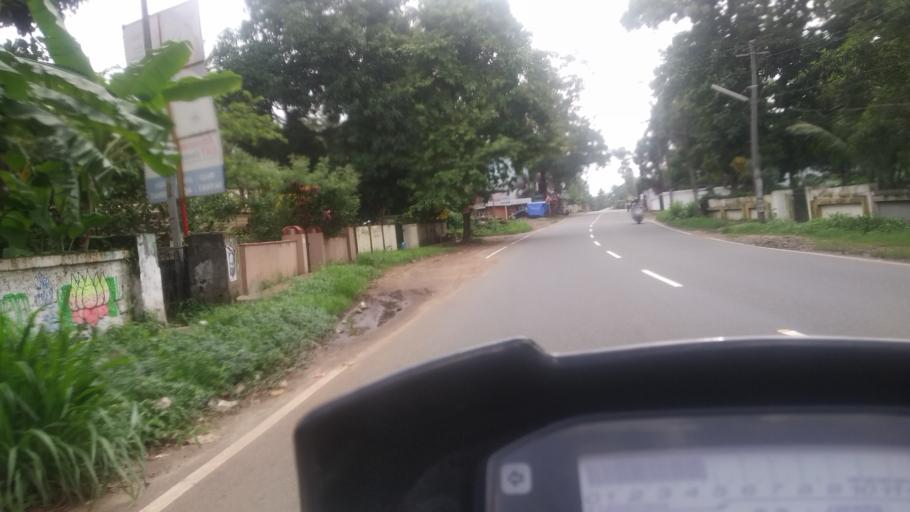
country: IN
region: Kerala
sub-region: Ernakulam
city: Aluva
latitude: 10.1263
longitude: 76.3223
